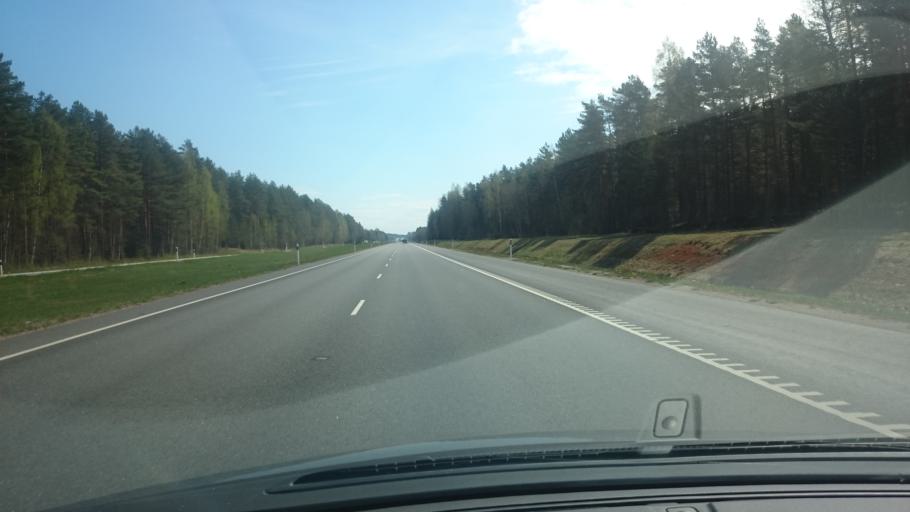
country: EE
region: Harju
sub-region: Loksa linn
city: Loksa
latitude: 59.4627
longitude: 25.6560
